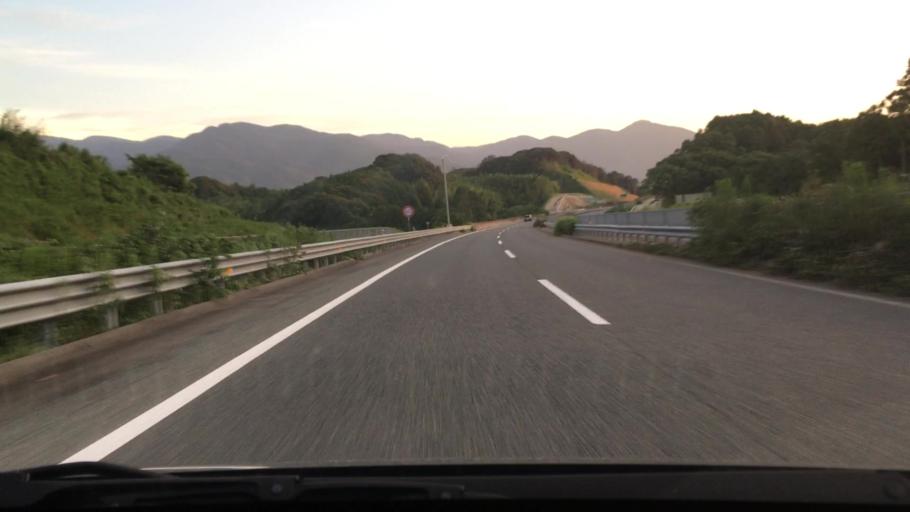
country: JP
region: Fukuoka
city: Maebaru-chuo
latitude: 33.5357
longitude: 130.1946
